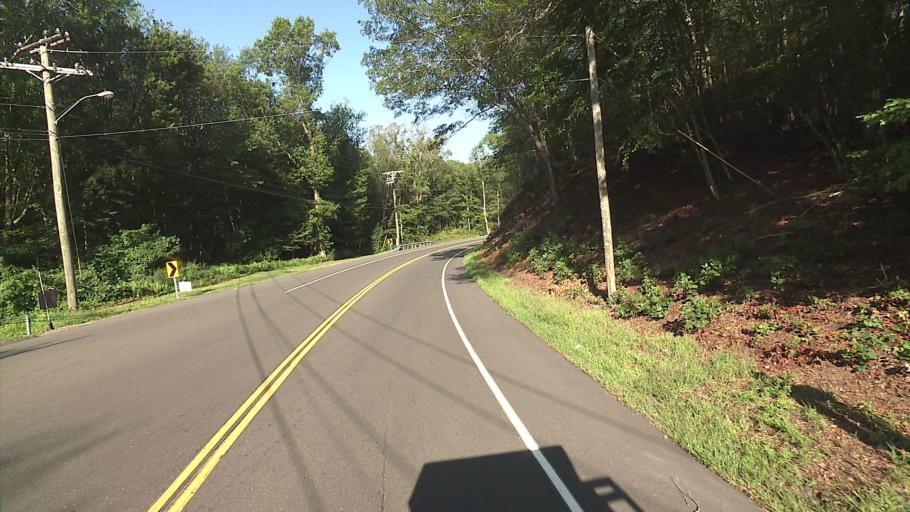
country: US
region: Connecticut
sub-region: New London County
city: Niantic
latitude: 41.3422
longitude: -72.2664
